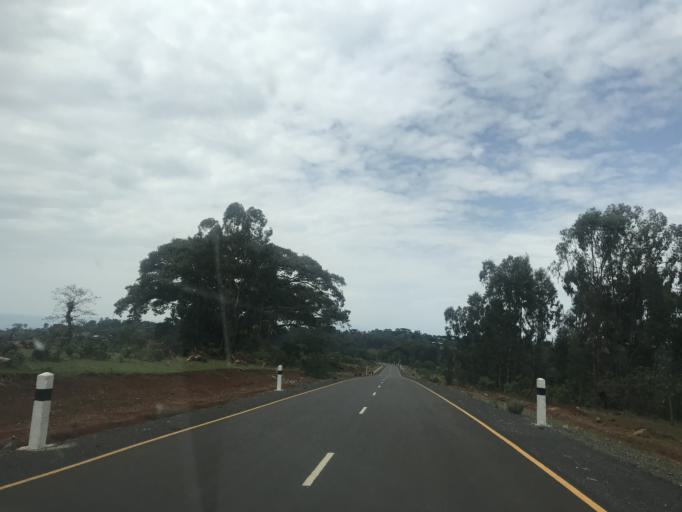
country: ET
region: Oromiya
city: Shambu
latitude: 9.8756
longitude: 36.6740
